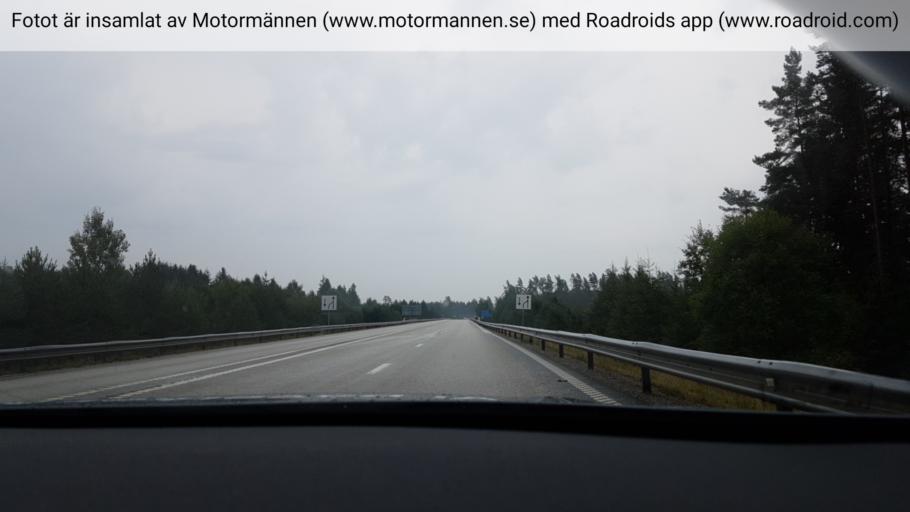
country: SE
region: Joenkoeping
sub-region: Jonkopings Kommun
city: Odensjo
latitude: 57.6190
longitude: 14.1958
